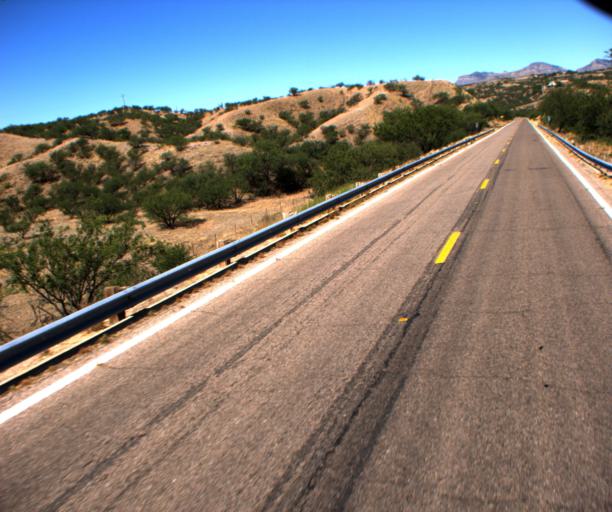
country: US
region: Arizona
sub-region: Santa Cruz County
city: Rio Rico
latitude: 31.4297
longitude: -110.9976
